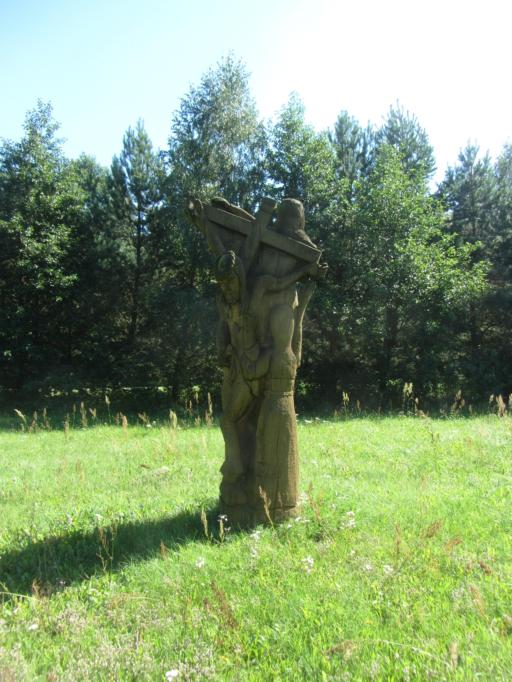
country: LT
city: Simnas
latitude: 54.2606
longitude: 23.6955
